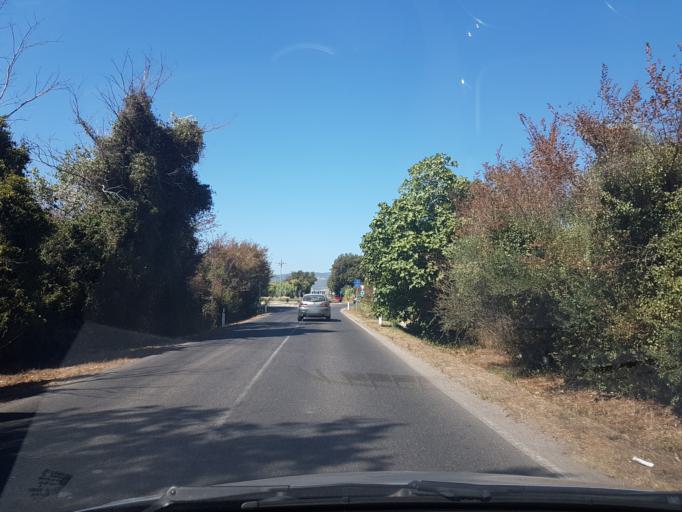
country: IT
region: Sardinia
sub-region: Provincia di Oristano
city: Nurachi
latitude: 39.9814
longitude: 8.5392
